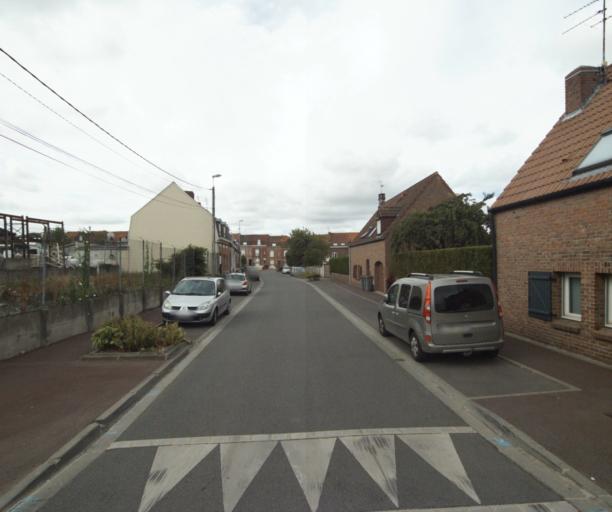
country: FR
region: Nord-Pas-de-Calais
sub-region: Departement du Nord
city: Linselles
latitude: 50.7357
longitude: 3.0758
